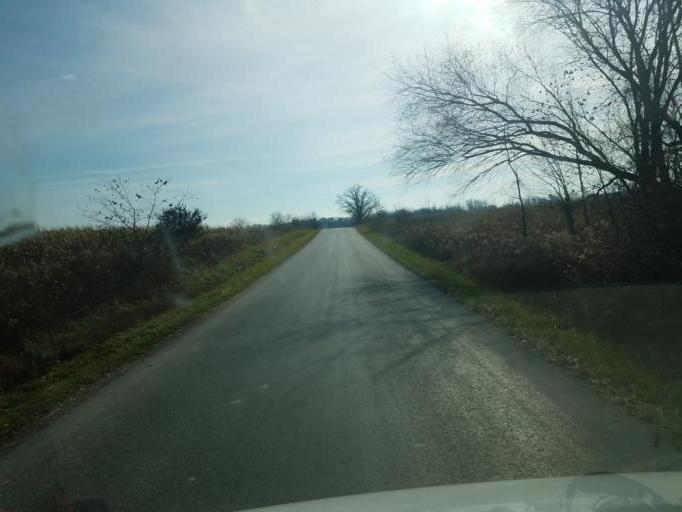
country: US
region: Ohio
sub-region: Hardin County
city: Kenton
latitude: 40.6183
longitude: -83.4386
